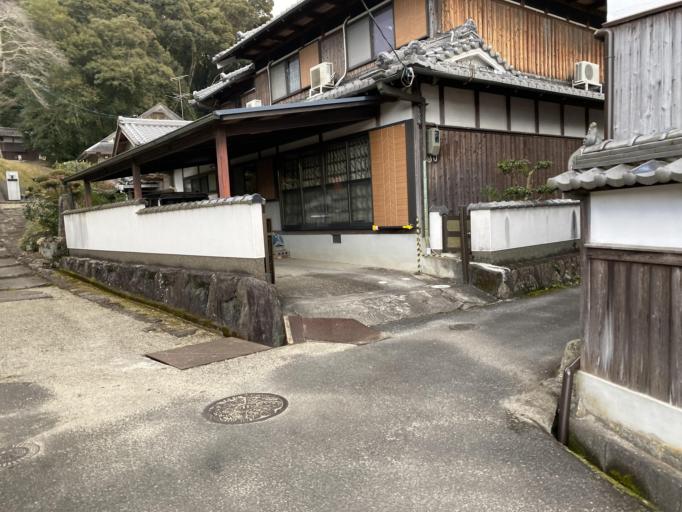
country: JP
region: Nara
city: Nara-shi
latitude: 34.7542
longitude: 135.8761
